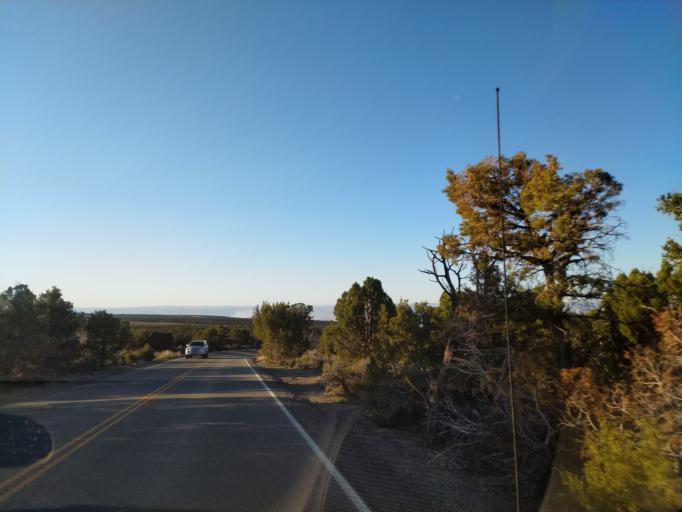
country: US
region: Colorado
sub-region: Mesa County
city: Redlands
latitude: 39.0225
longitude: -108.6599
